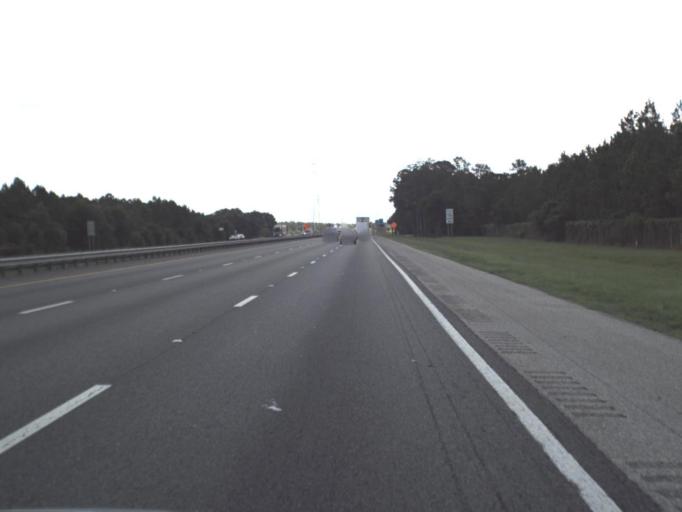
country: US
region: Florida
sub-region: Flagler County
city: Palm Coast
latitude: 29.6680
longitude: -81.2977
